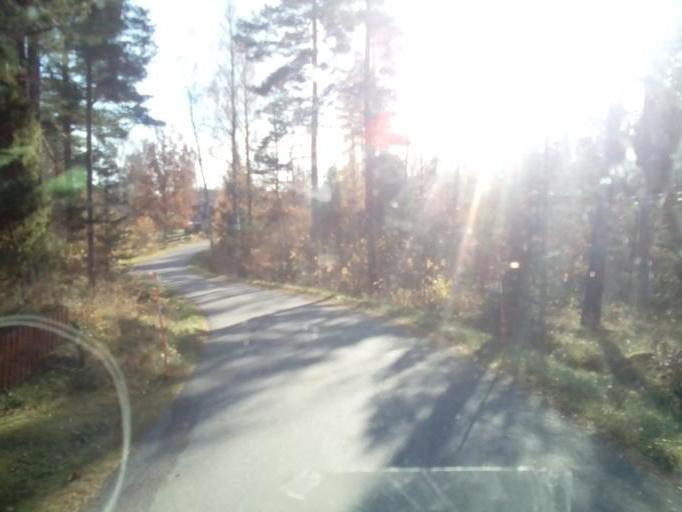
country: SE
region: Kalmar
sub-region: Vasterviks Kommun
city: Ankarsrum
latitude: 57.8037
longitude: 16.1688
